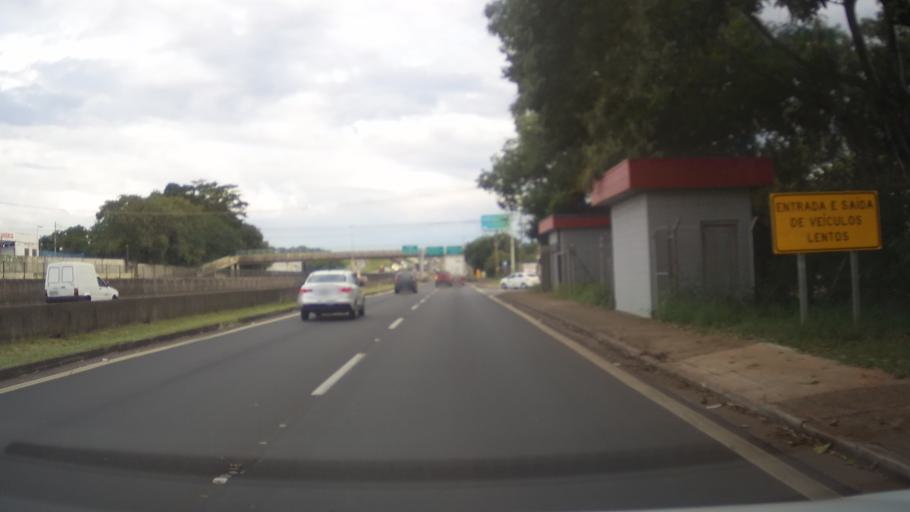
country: BR
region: Sao Paulo
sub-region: Campinas
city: Campinas
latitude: -22.8905
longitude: -47.1127
